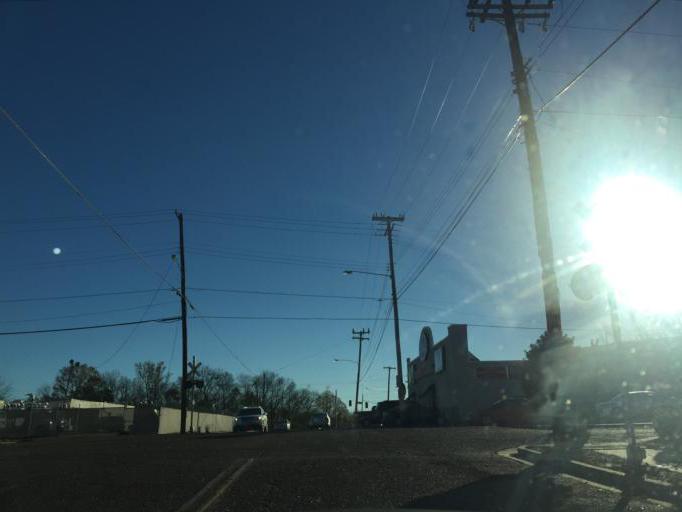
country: US
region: Mississippi
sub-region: Hinds County
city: Jackson
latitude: 32.2902
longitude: -90.1810
